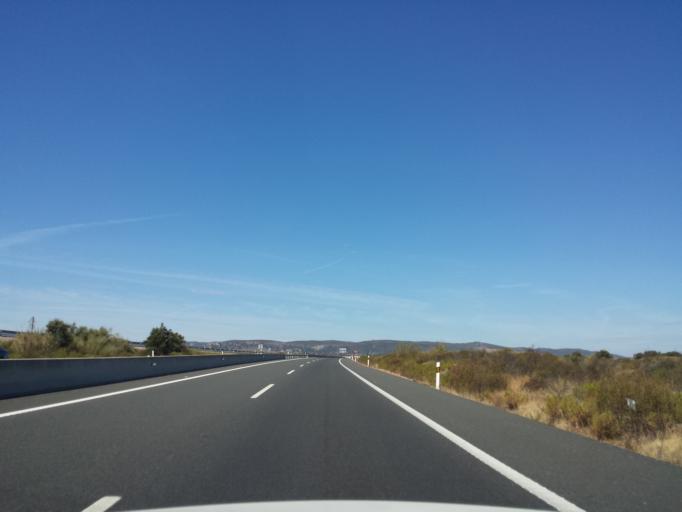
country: ES
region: Extremadura
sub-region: Provincia de Caceres
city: Almaraz
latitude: 39.7897
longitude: -5.7001
